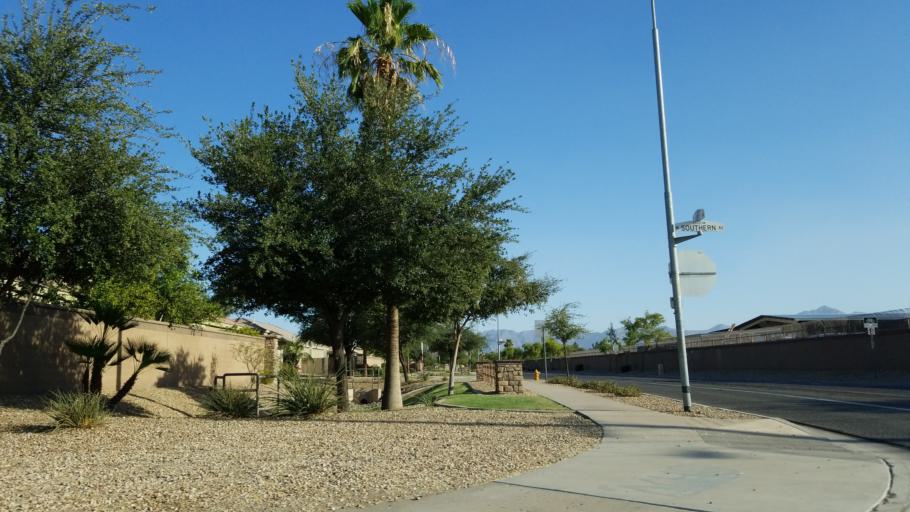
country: US
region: Arizona
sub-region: Maricopa County
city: Laveen
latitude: 33.3918
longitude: -112.2074
